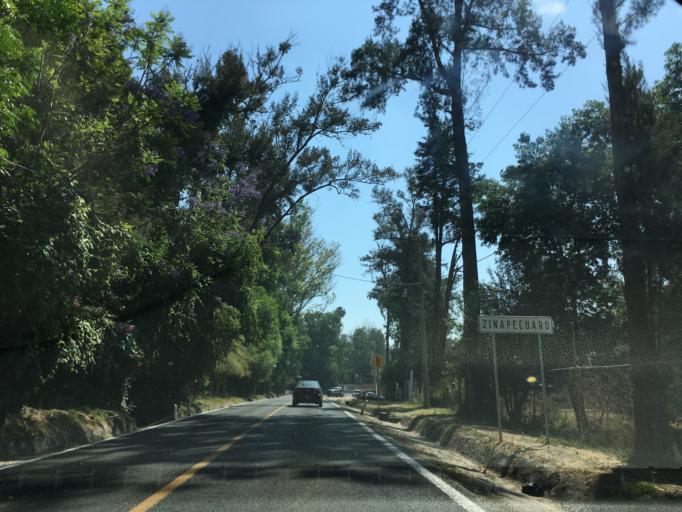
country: MX
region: Michoacan
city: Zinapecuaro
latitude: 19.8651
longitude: -100.8410
